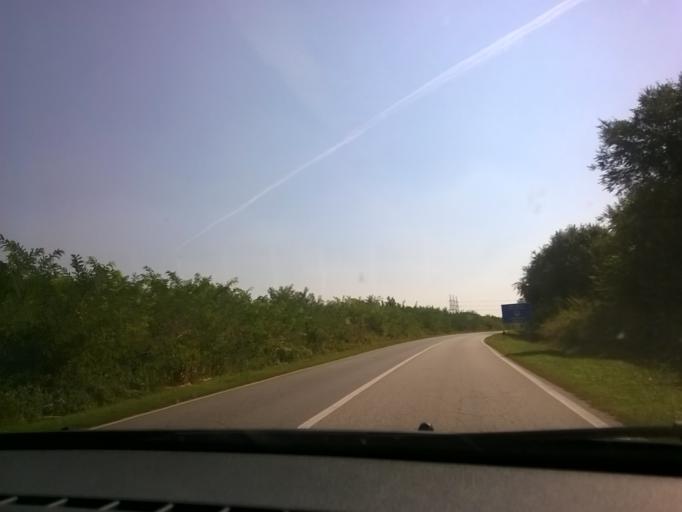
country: RS
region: Autonomna Pokrajina Vojvodina
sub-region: Juznobanatski Okrug
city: Vrsac
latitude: 45.1252
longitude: 21.2750
